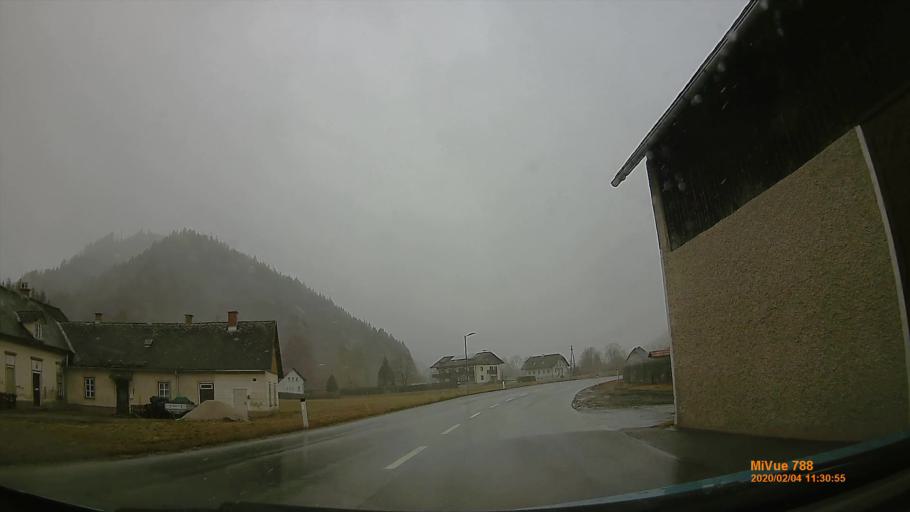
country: AT
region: Styria
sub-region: Politischer Bezirk Bruck-Muerzzuschlag
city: Neuberg an der Muerz
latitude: 47.6567
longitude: 15.5957
